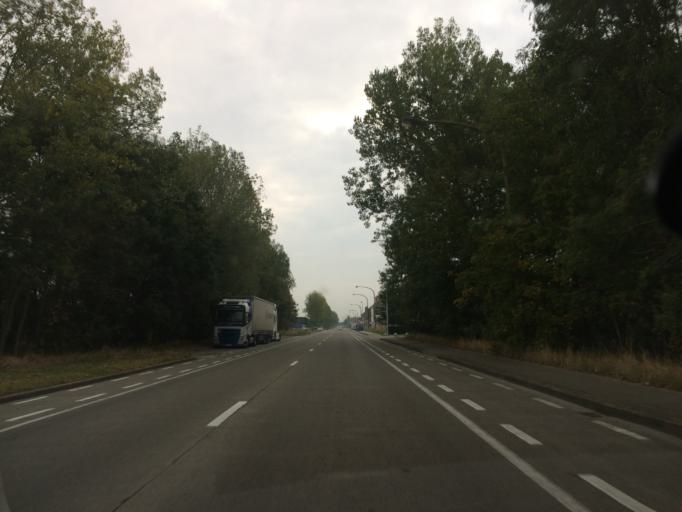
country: BE
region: Flanders
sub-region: Provincie West-Vlaanderen
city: Bredene
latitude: 51.2095
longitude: 2.9634
